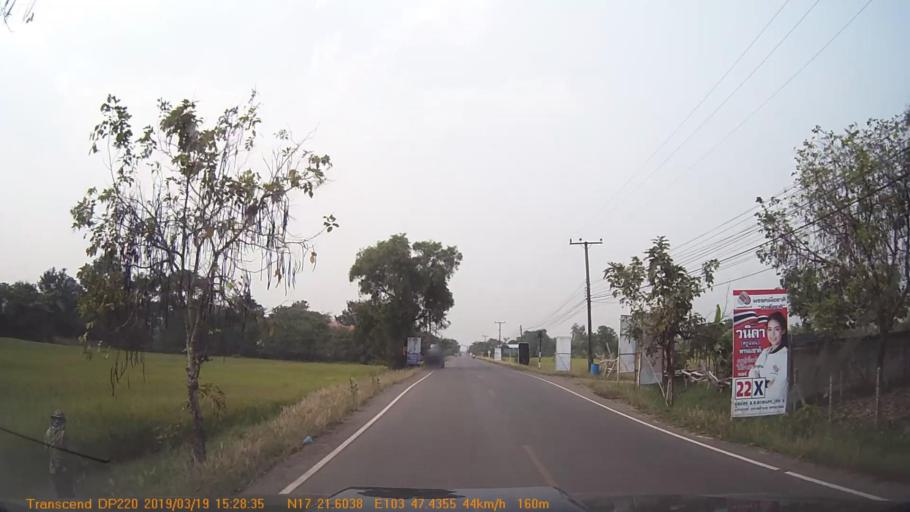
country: TH
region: Sakon Nakhon
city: Phanna Nikhom
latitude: 17.3603
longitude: 103.7905
